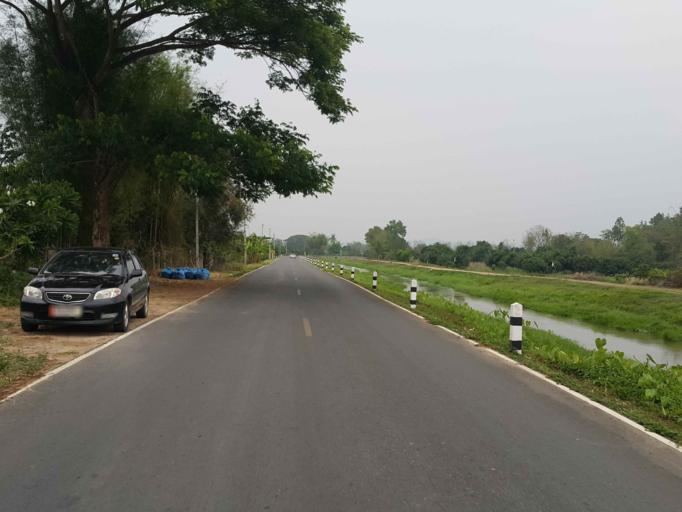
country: TH
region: Chiang Mai
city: Mae Taeng
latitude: 18.9871
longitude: 98.9792
